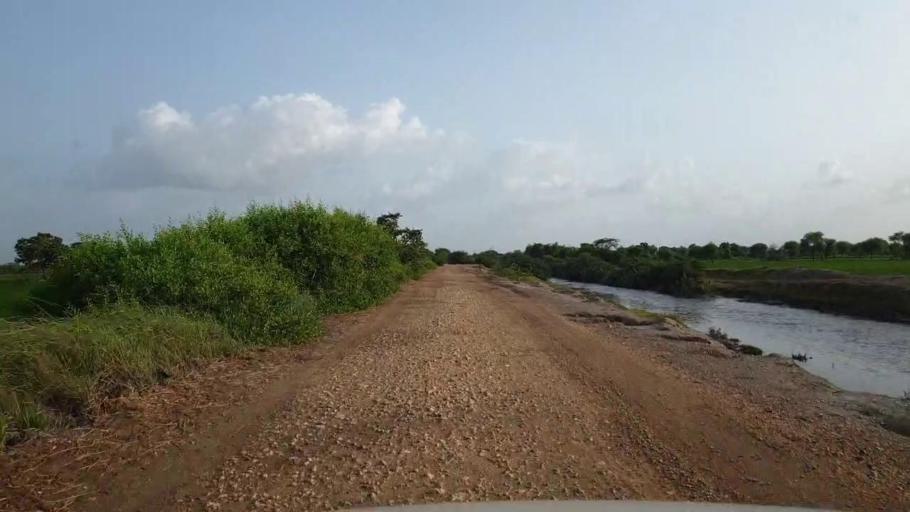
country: PK
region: Sindh
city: Kario
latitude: 24.8275
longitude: 68.6491
